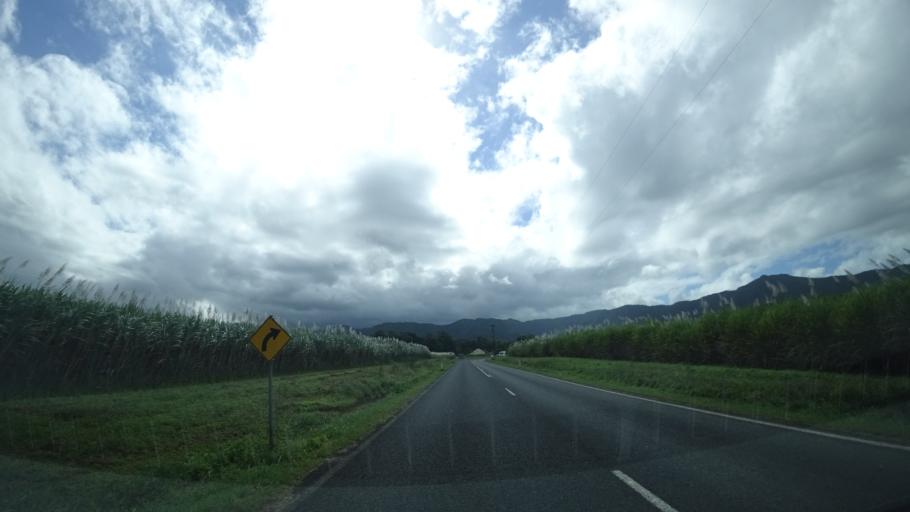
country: AU
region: Queensland
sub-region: Cairns
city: Port Douglas
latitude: -16.2652
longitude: 145.3924
